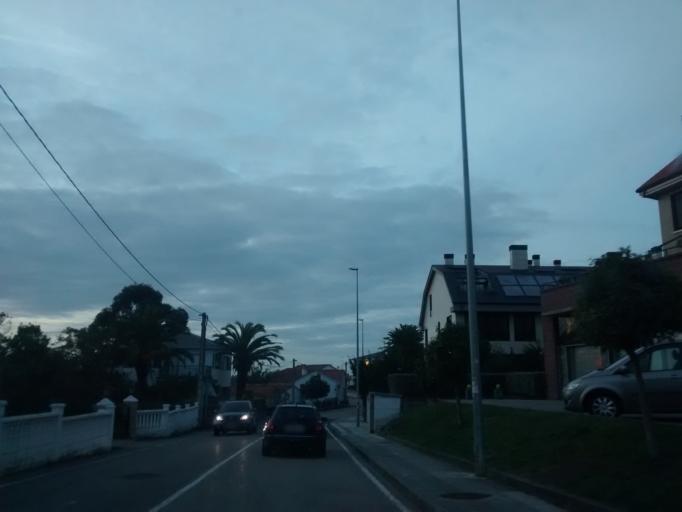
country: ES
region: Cantabria
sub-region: Provincia de Cantabria
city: Santa Cruz de Bezana
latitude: 43.4289
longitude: -3.9433
